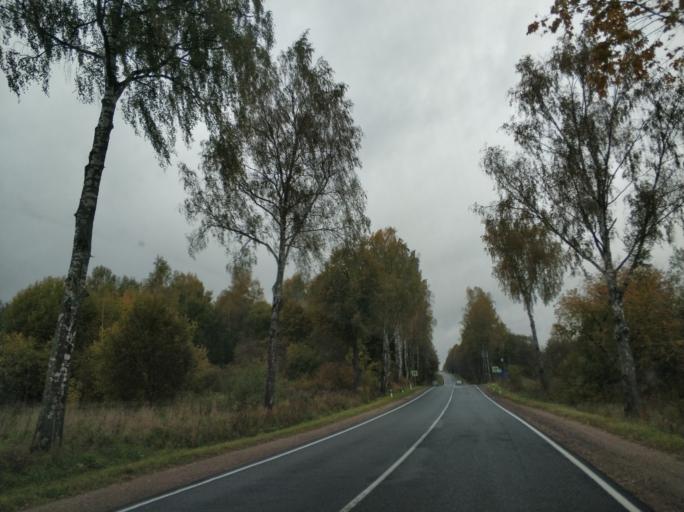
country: RU
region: Pskov
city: Opochka
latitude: 56.5550
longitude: 28.6325
